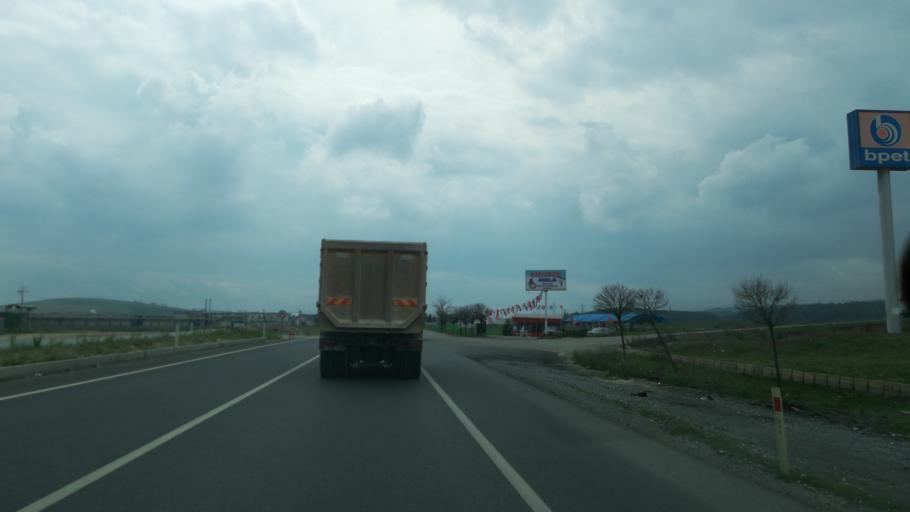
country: TR
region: Kahramanmaras
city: Turkoglu
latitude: 37.4404
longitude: 36.8866
